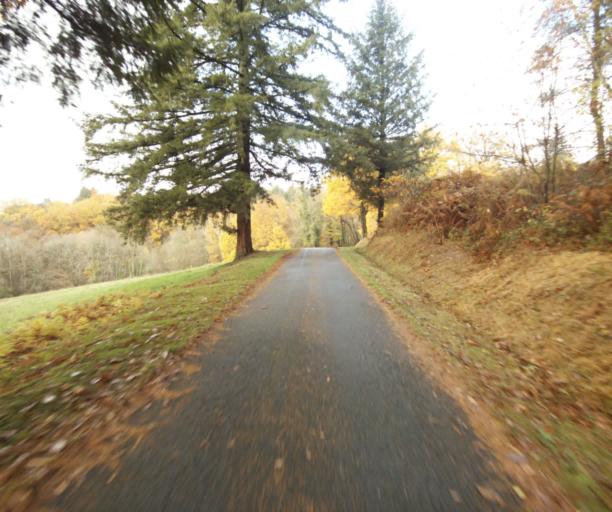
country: FR
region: Limousin
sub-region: Departement de la Correze
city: Cornil
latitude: 45.2235
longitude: 1.6571
